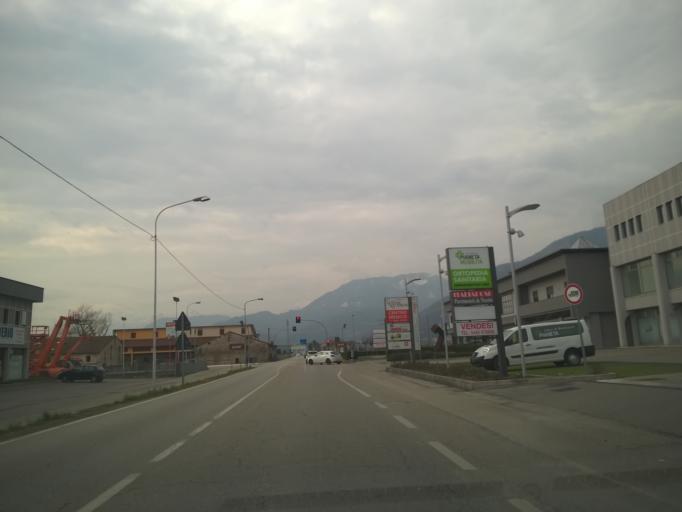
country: IT
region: Veneto
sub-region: Provincia di Vicenza
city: Zane
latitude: 45.7243
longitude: 11.4271
